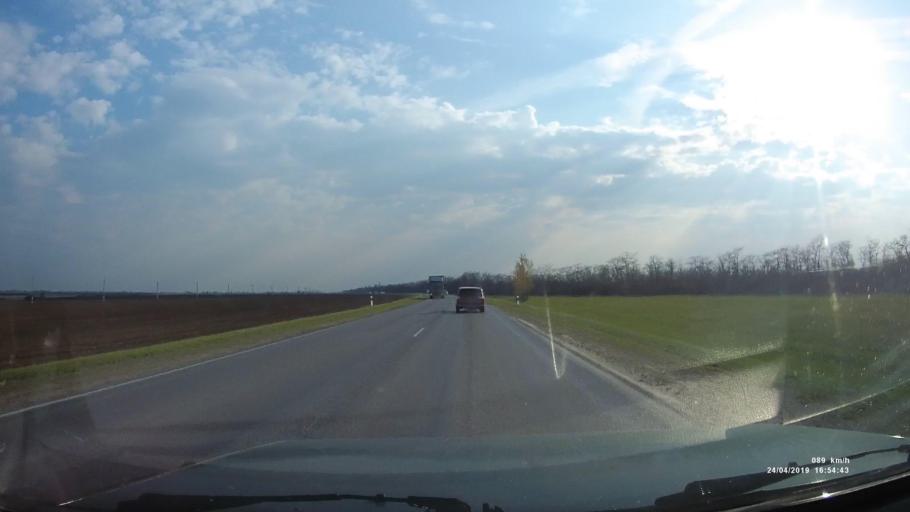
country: RU
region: Rostov
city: Proletarsk
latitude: 46.6731
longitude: 41.6961
